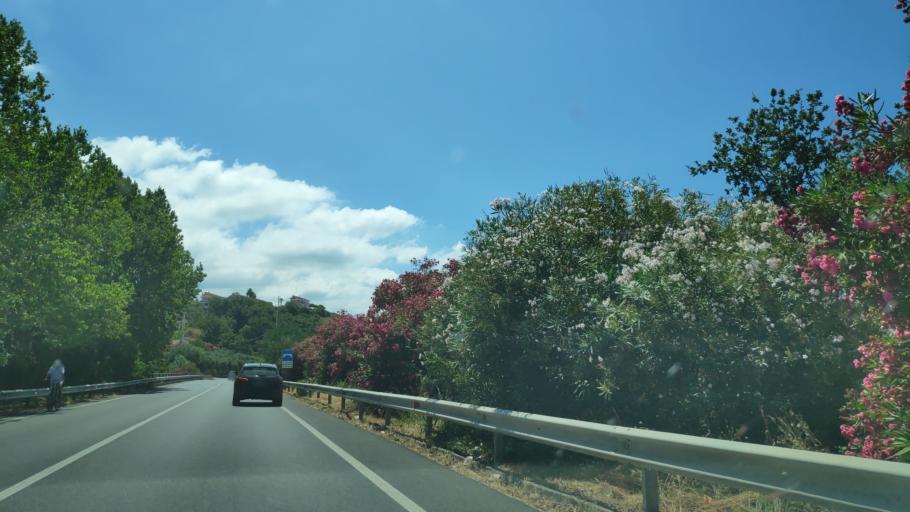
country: IT
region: Calabria
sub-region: Provincia di Cosenza
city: Diamante
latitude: 39.6753
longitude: 15.8274
